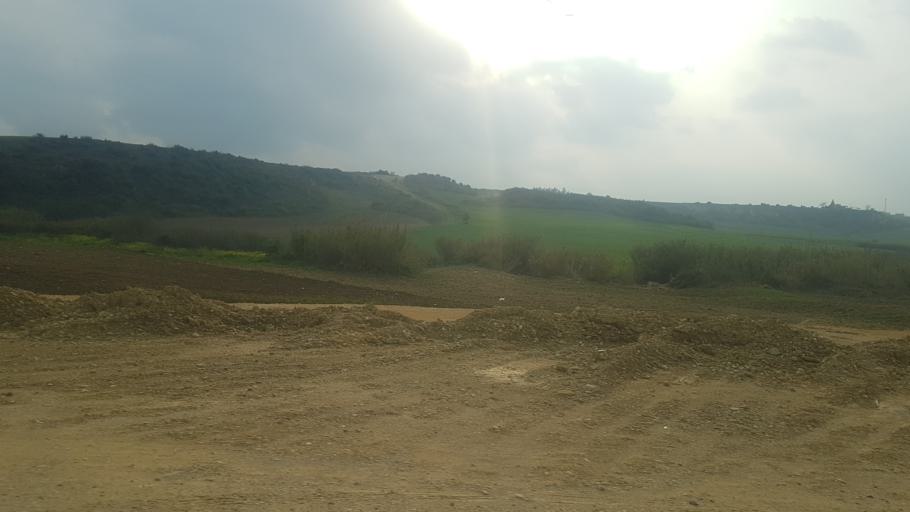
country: TR
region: Adana
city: Seyhan
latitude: 37.0434
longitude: 35.2128
